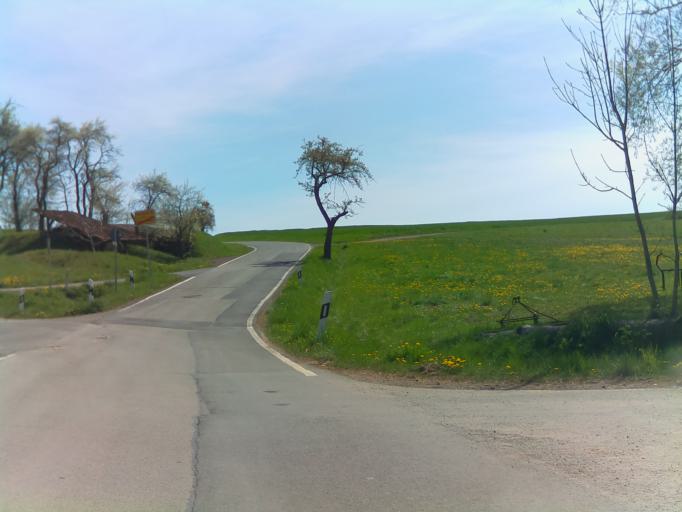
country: DE
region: Thuringia
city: Veilsdorf
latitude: 50.3583
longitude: 10.7697
